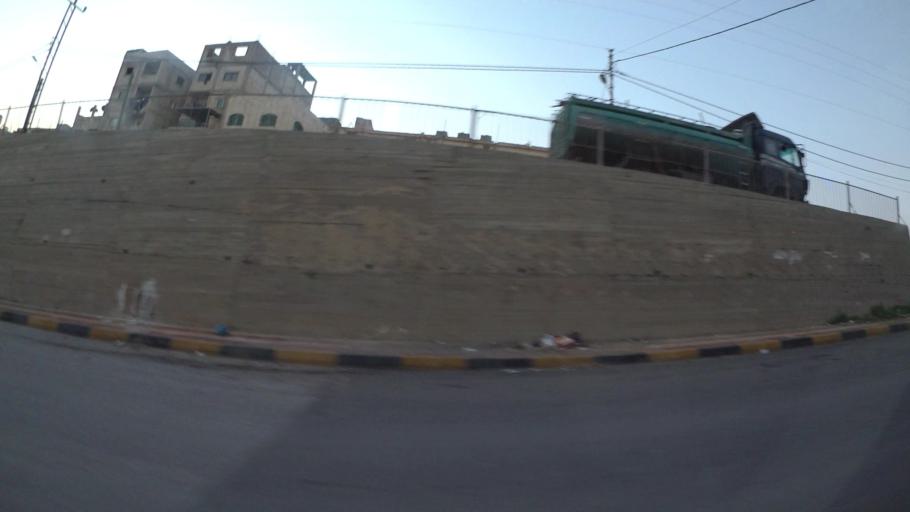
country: JO
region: Amman
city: Amman
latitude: 31.9976
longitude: 35.9782
